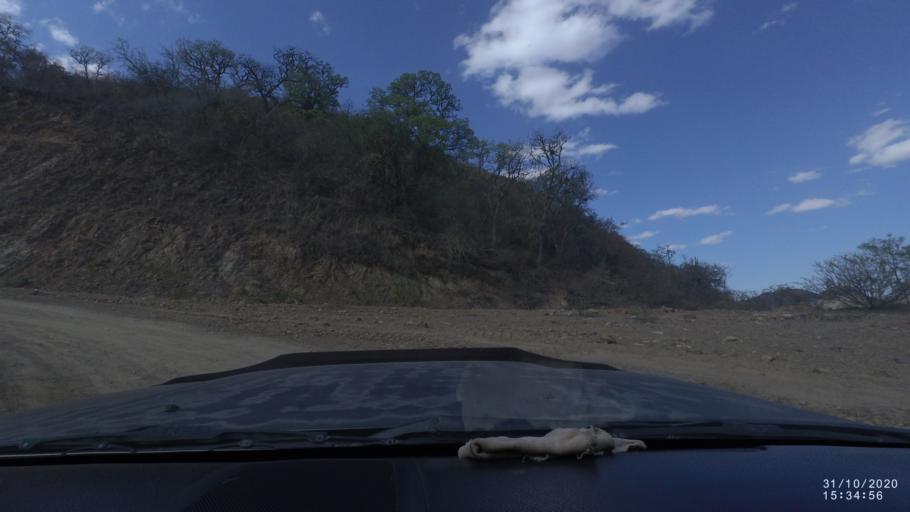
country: BO
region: Chuquisaca
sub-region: Provincia Zudanez
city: Mojocoya
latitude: -18.3413
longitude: -64.7519
